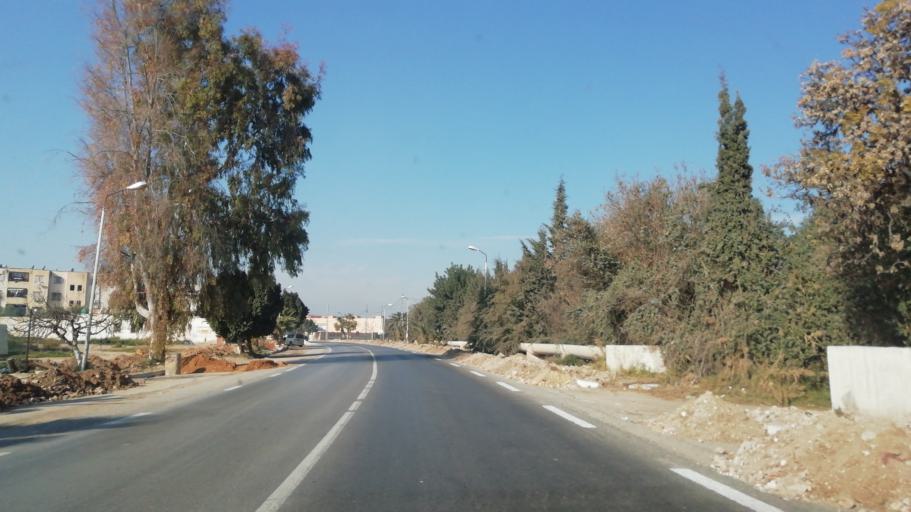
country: DZ
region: Relizane
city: Relizane
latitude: 35.7339
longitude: 0.4680
